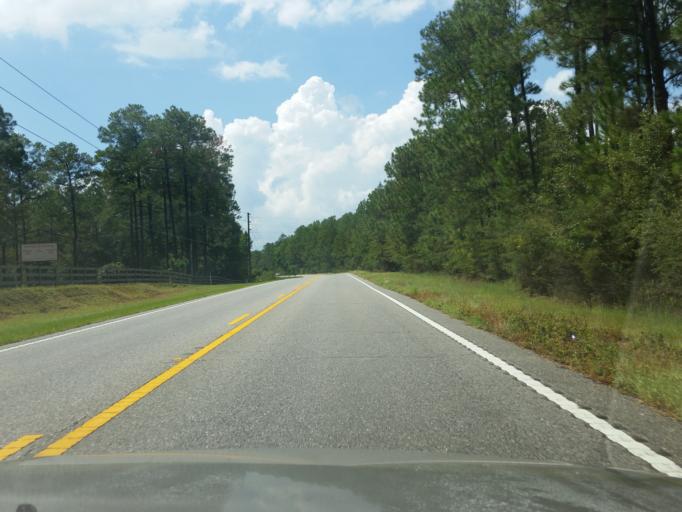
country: US
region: Alabama
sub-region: Baldwin County
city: Elberta
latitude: 30.5305
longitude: -87.5181
